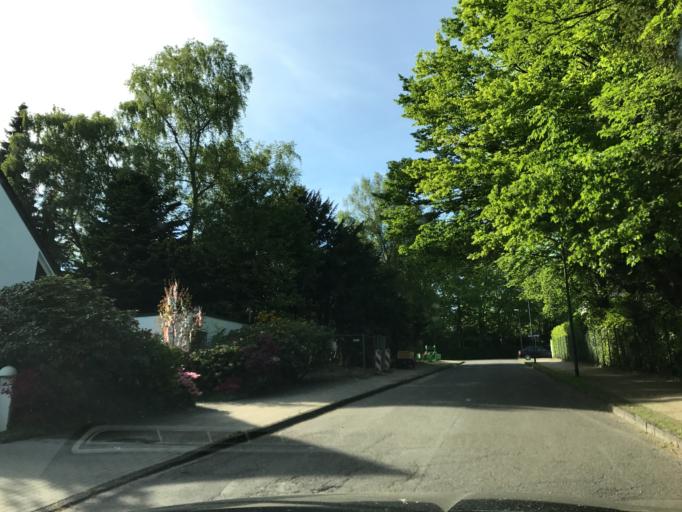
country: DE
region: North Rhine-Westphalia
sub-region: Regierungsbezirk Dusseldorf
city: Essen
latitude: 51.4034
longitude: 6.9822
